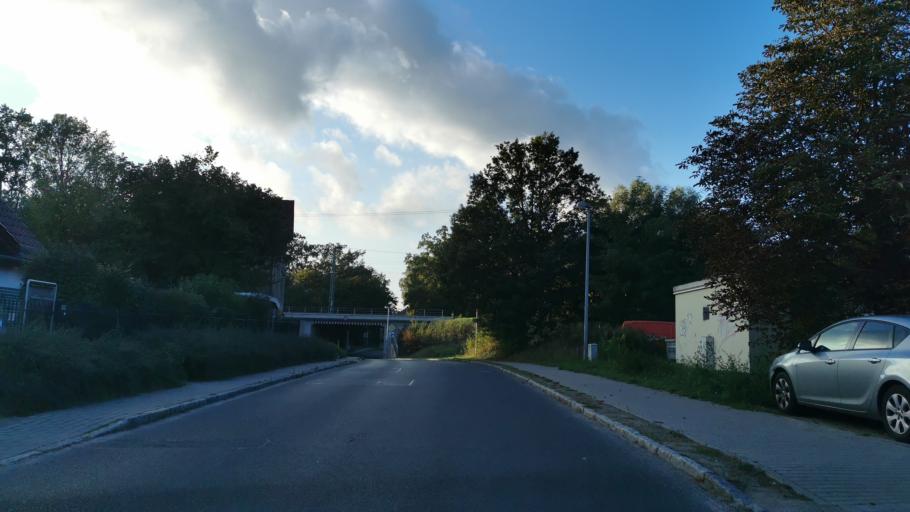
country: DE
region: Brandenburg
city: Michendorf
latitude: 52.3106
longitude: 13.0228
